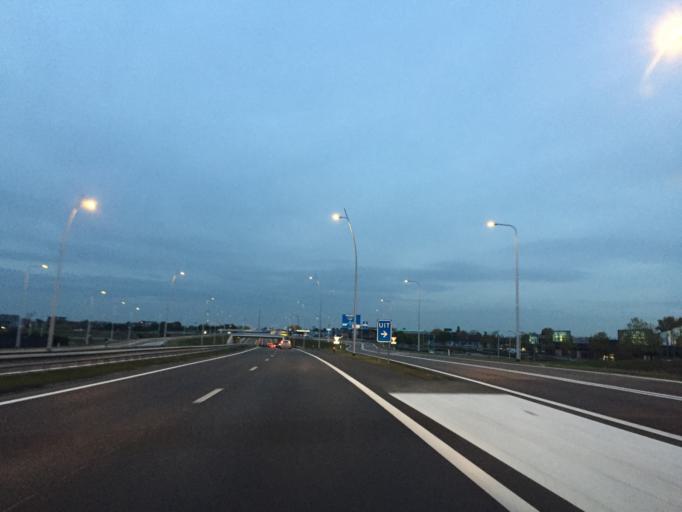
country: NL
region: North Brabant
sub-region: Gemeente Waalwijk
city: Waalwijk
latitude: 51.6732
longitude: 5.0546
